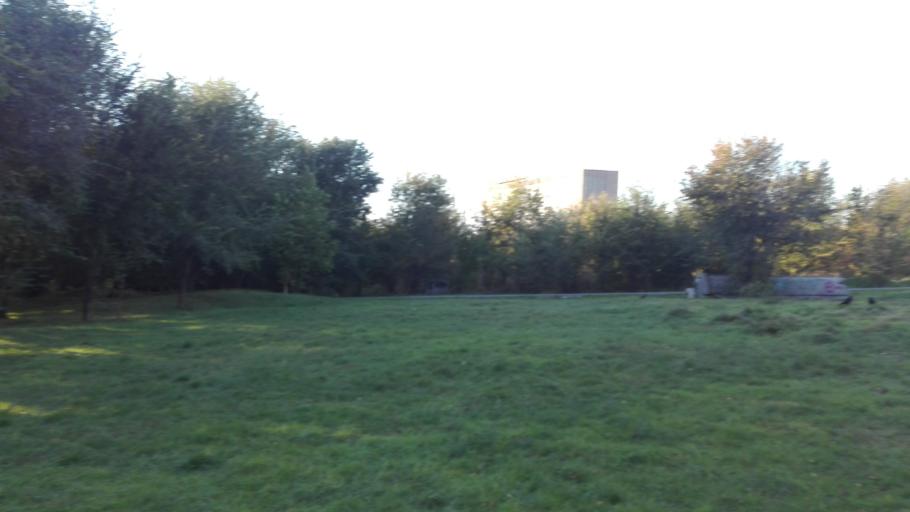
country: RU
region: Rostov
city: Rostov-na-Donu
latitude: 47.2173
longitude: 39.6304
